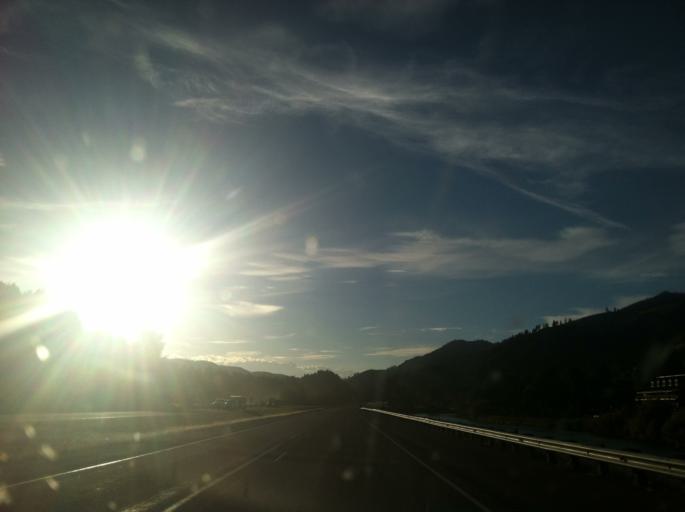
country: US
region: Montana
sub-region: Missoula County
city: Clinton
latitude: 46.6968
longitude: -113.4213
